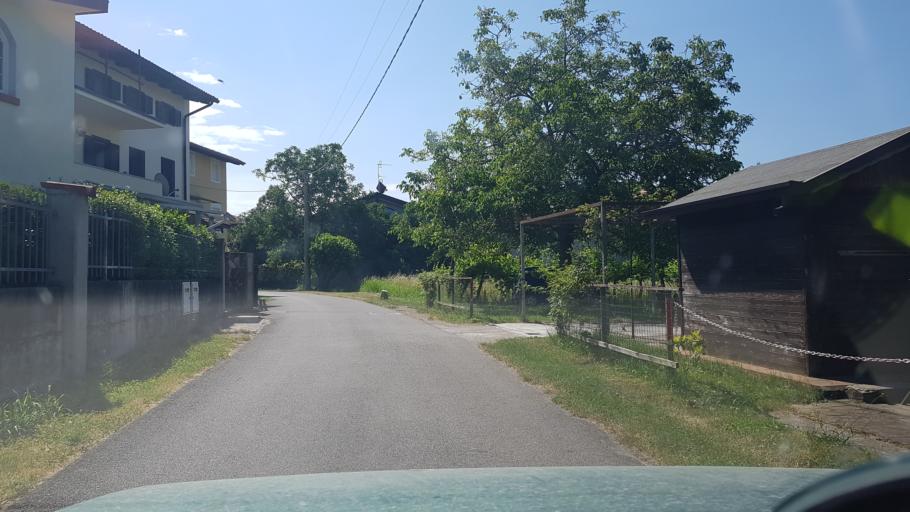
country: SI
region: Nova Gorica
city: Nova Gorica
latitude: 45.9620
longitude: 13.6303
